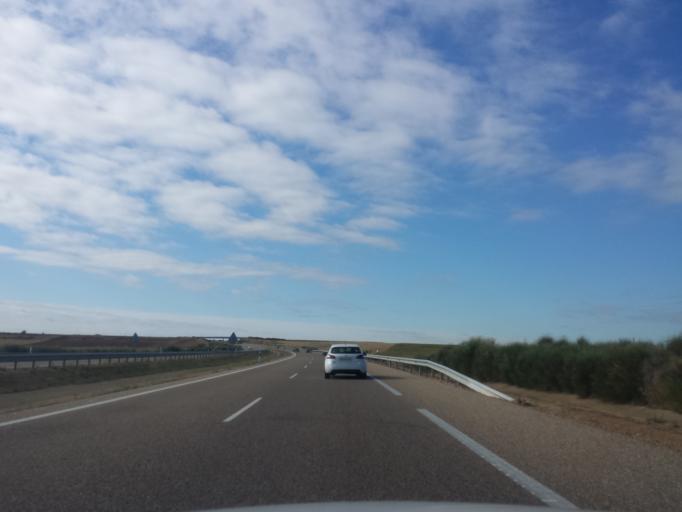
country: ES
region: Castille and Leon
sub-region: Provincia de Leon
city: Villademor de la Vega
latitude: 42.2855
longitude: -5.5909
